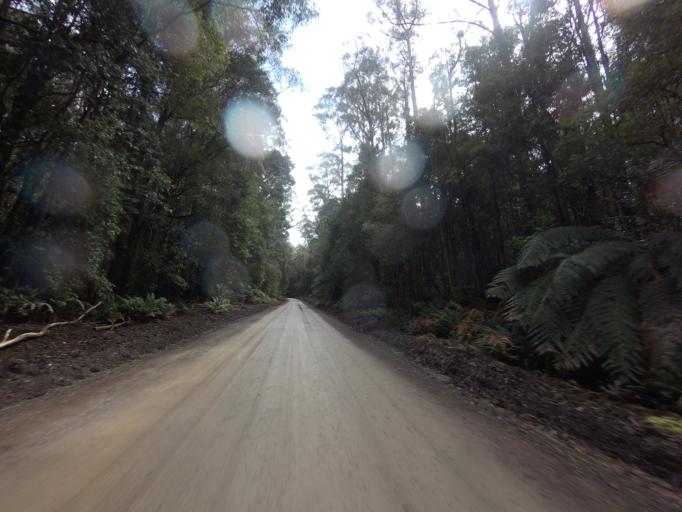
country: AU
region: Tasmania
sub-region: Huon Valley
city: Geeveston
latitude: -43.3890
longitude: 146.8509
